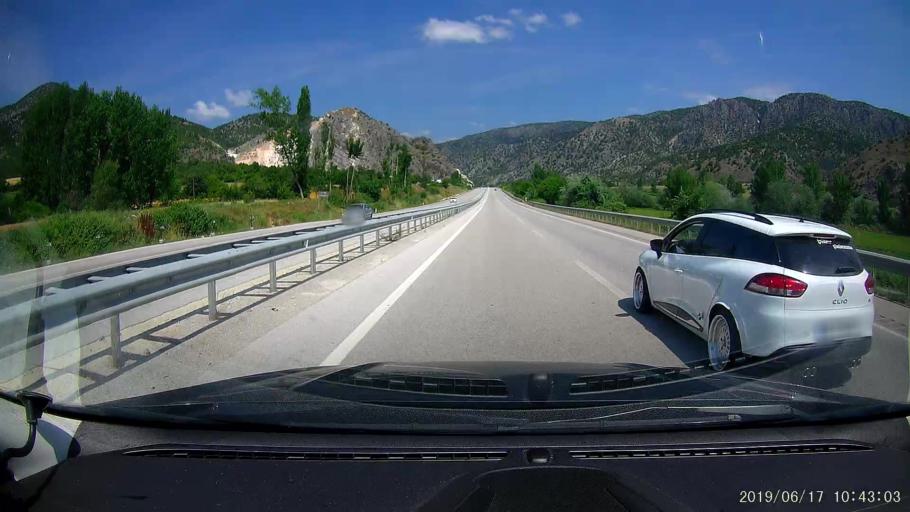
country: TR
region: Corum
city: Kargi
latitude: 41.0574
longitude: 34.5424
